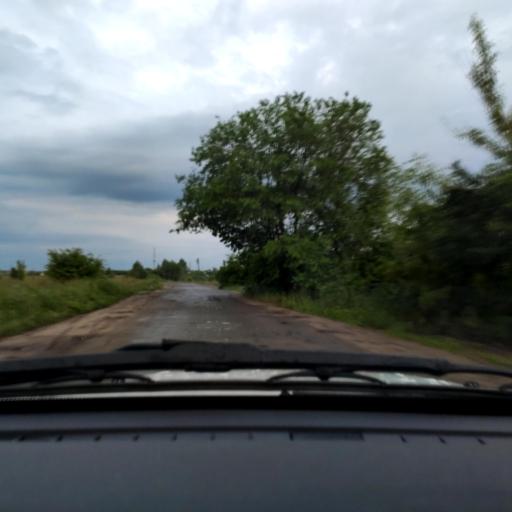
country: RU
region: Voronezj
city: Maslovka
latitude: 51.5179
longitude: 39.2244
